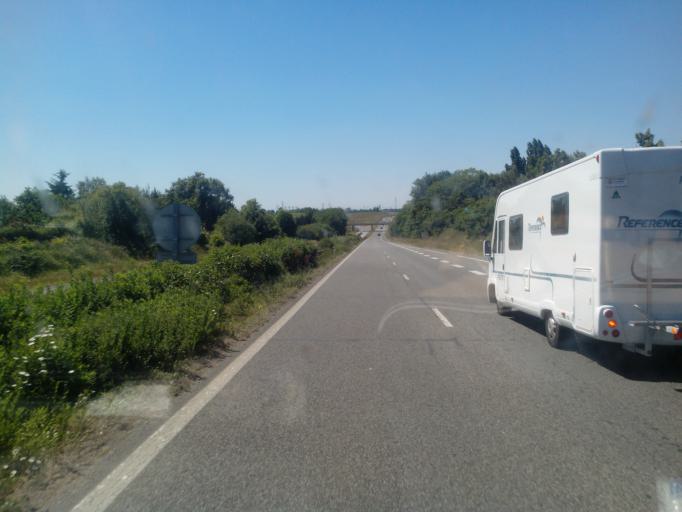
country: FR
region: Brittany
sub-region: Departement d'Ille-et-Vilaine
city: Vezin-le-Coquet
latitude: 48.1214
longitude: -1.7261
